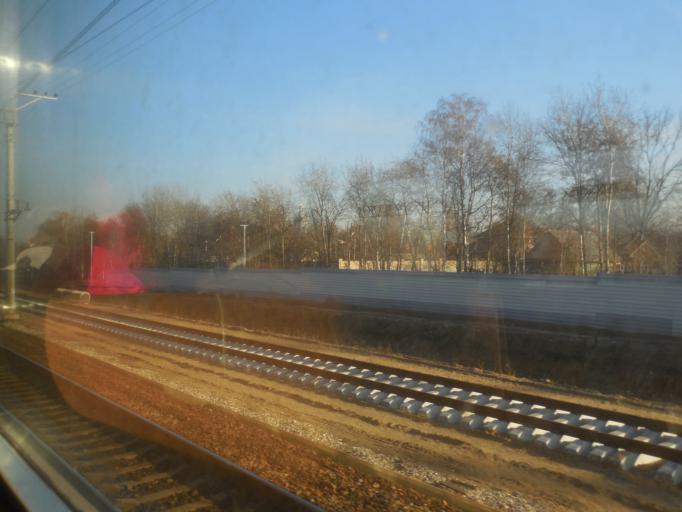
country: RU
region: Moskovskaya
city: Reutov
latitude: 55.7588
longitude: 37.8921
